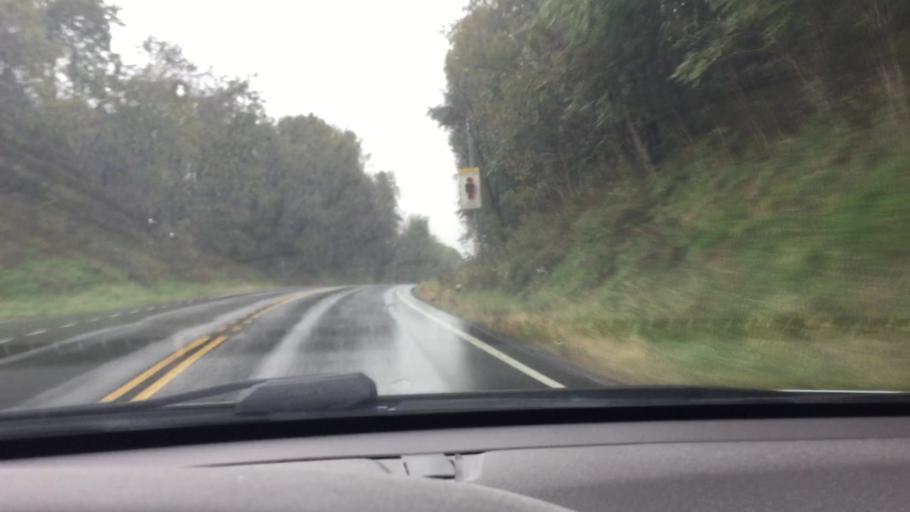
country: US
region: Pennsylvania
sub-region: Westmoreland County
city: Fellsburg
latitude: 40.1733
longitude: -79.8203
